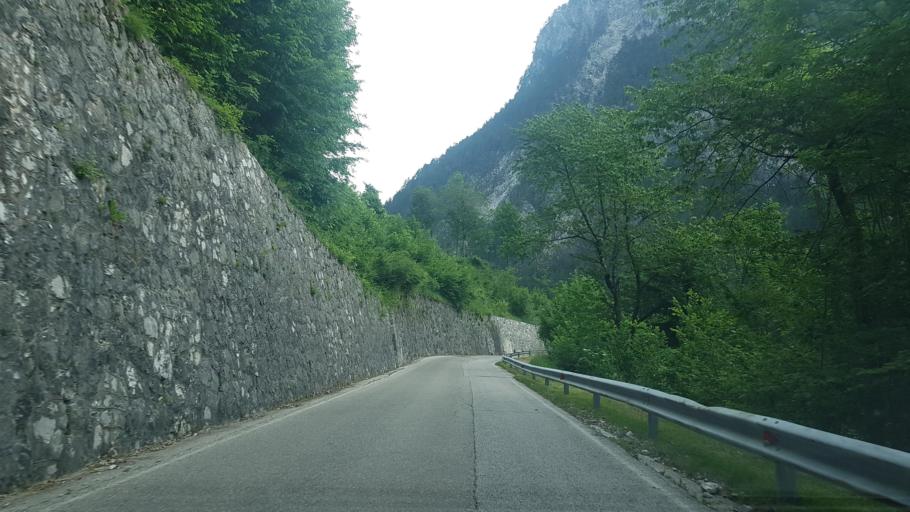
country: IT
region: Friuli Venezia Giulia
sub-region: Provincia di Udine
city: Pontebba
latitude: 46.5213
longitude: 13.3000
